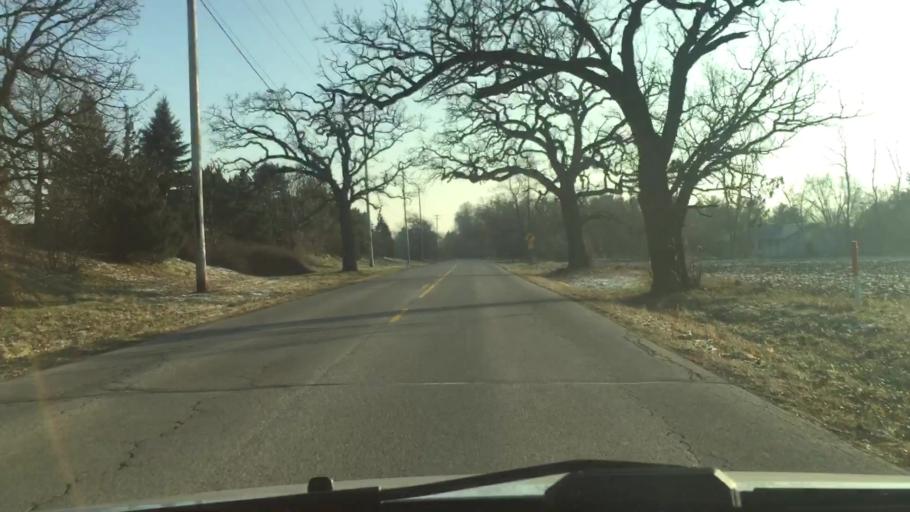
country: US
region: Wisconsin
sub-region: Waukesha County
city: Dousman
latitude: 43.0596
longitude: -88.4815
